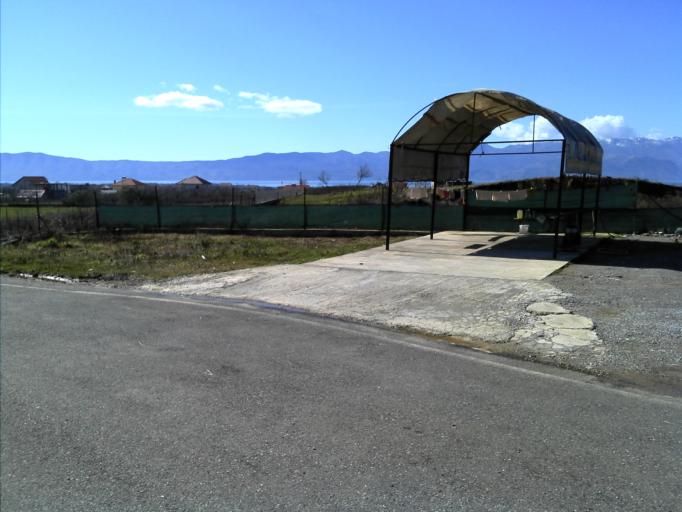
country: AL
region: Shkoder
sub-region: Rrethi i Malesia e Madhe
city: Koplik
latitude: 42.1969
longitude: 19.4555
